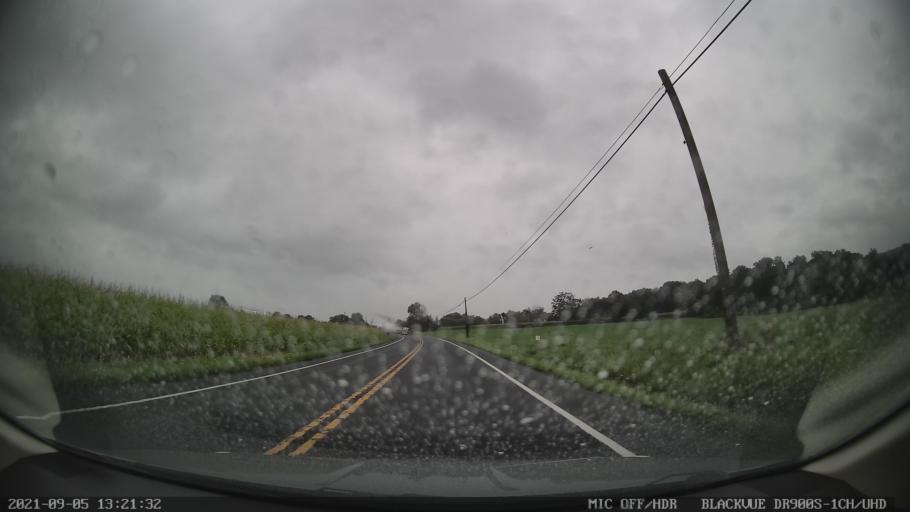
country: US
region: Pennsylvania
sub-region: Berks County
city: Topton
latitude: 40.4909
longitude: -75.7180
